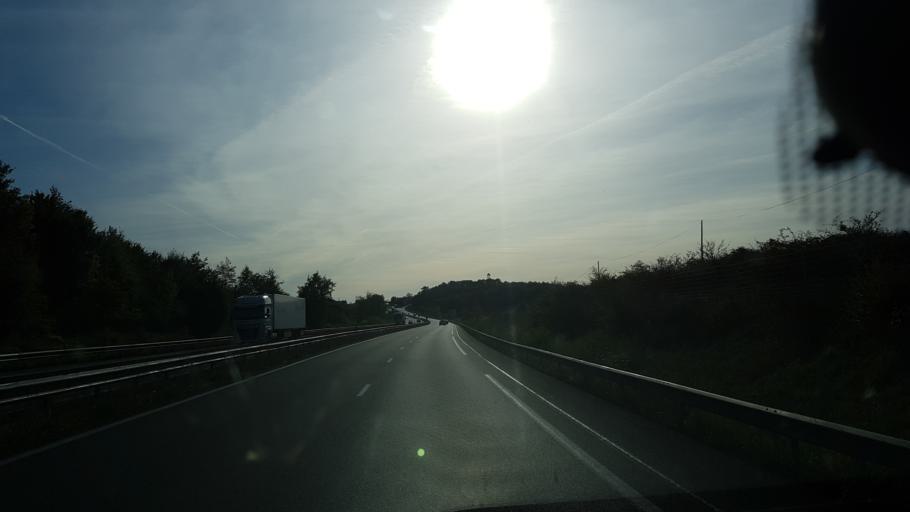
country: FR
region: Poitou-Charentes
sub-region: Departement de la Charente-Maritime
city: Montlieu-la-Garde
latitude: 45.2515
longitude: -0.2626
